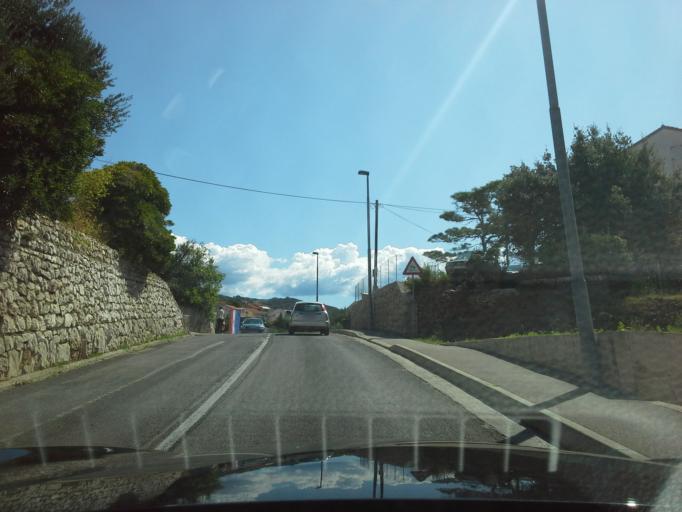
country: HR
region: Primorsko-Goranska
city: Banjol
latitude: 44.7605
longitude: 14.7652
